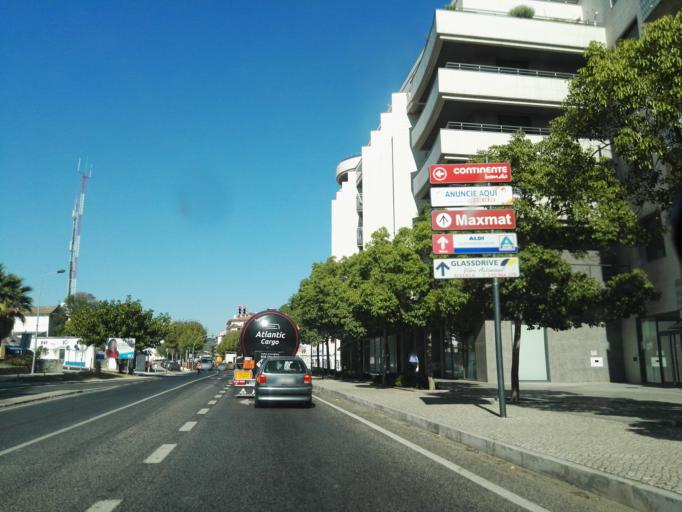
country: PT
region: Lisbon
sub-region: Vila Franca de Xira
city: Sobralinho
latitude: 38.8959
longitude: -9.0391
